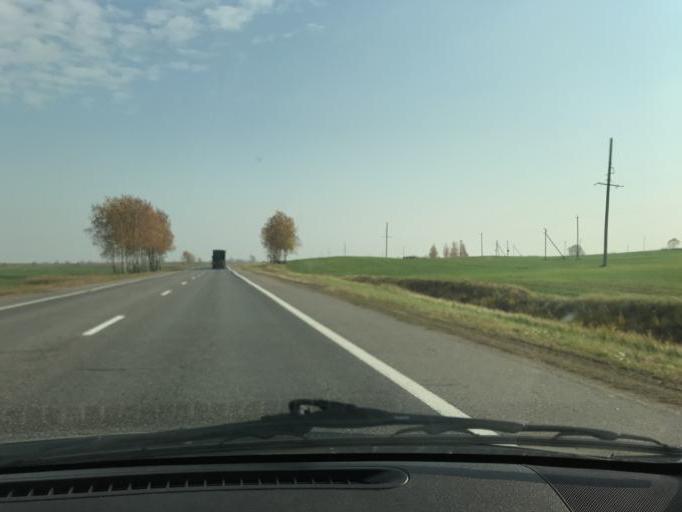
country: BY
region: Vitebsk
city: Chashniki
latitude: 55.0135
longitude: 29.1078
